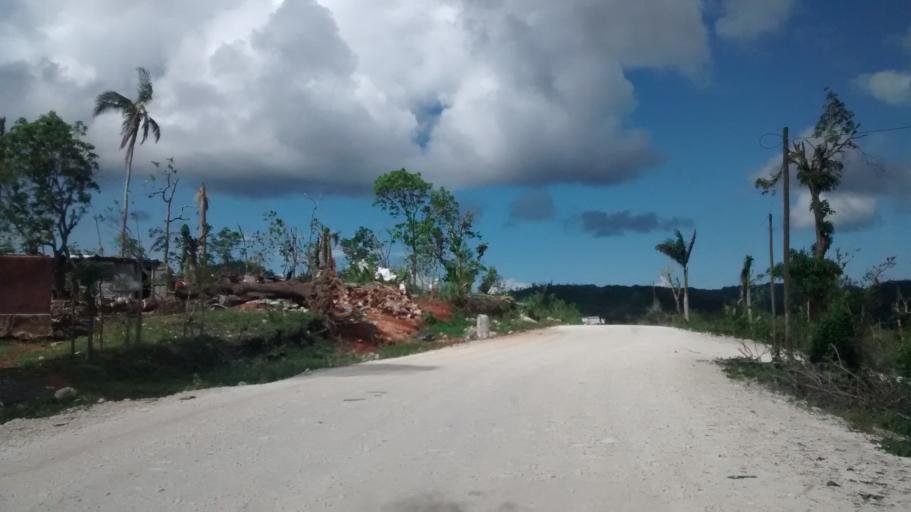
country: HT
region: Grandans
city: Corail
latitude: 18.5345
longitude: -73.9979
